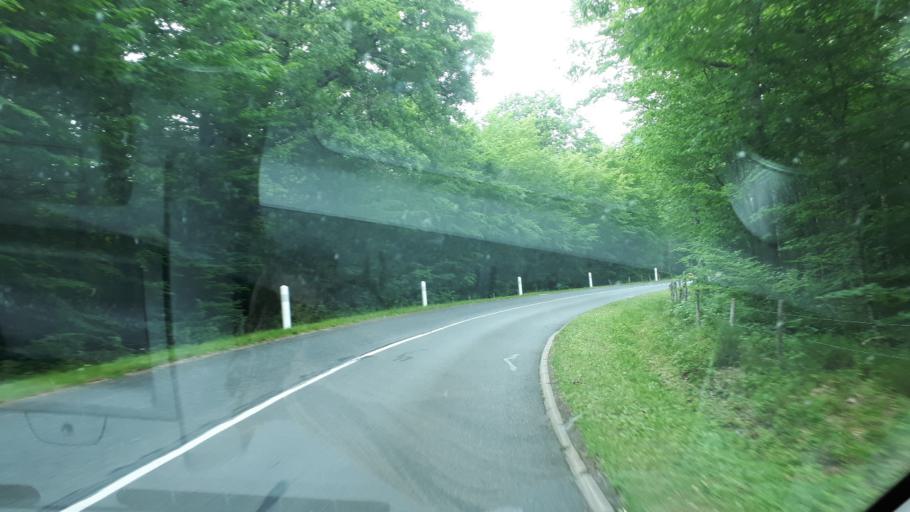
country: FR
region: Centre
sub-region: Departement du Loir-et-Cher
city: Villefranche-sur-Cher
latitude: 47.2250
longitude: 1.7674
